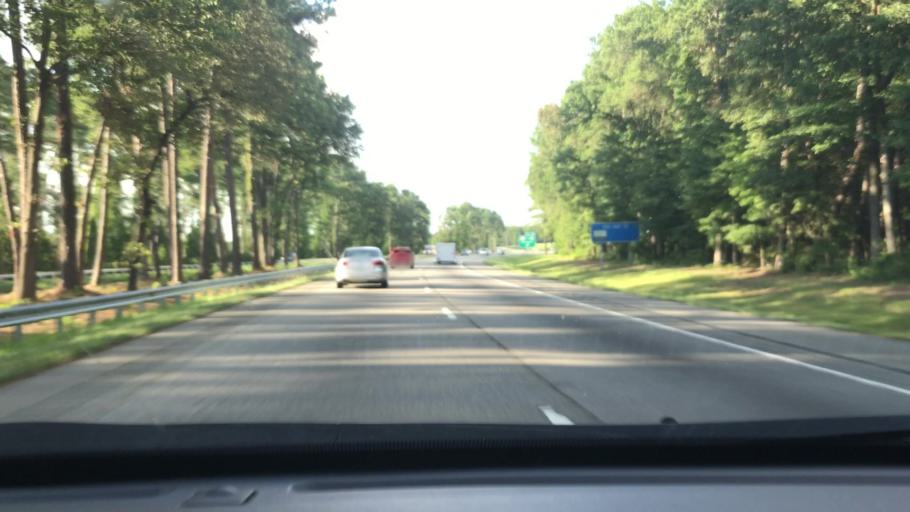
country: US
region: North Carolina
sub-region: Robeson County
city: Saint Pauls
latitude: 34.8282
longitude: -78.9821
